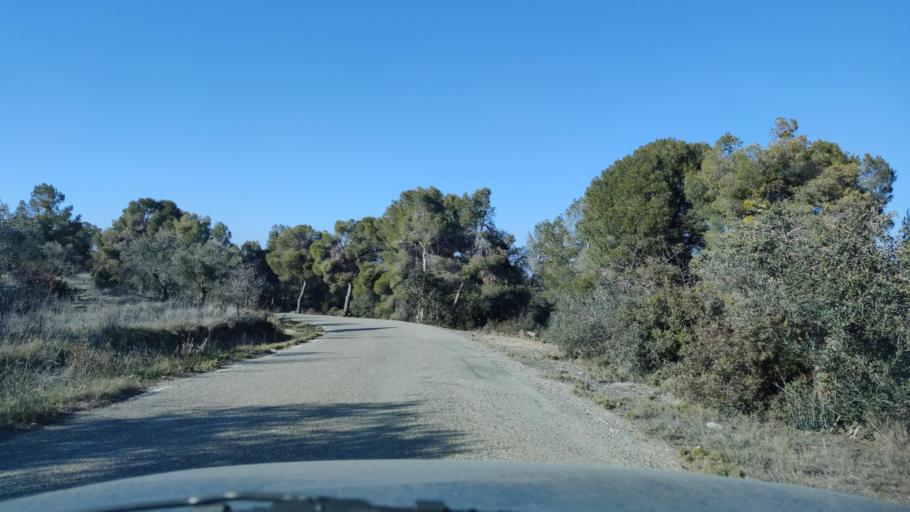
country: ES
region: Catalonia
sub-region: Provincia de Lleida
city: Torrebesses
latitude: 41.3992
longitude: 0.5653
